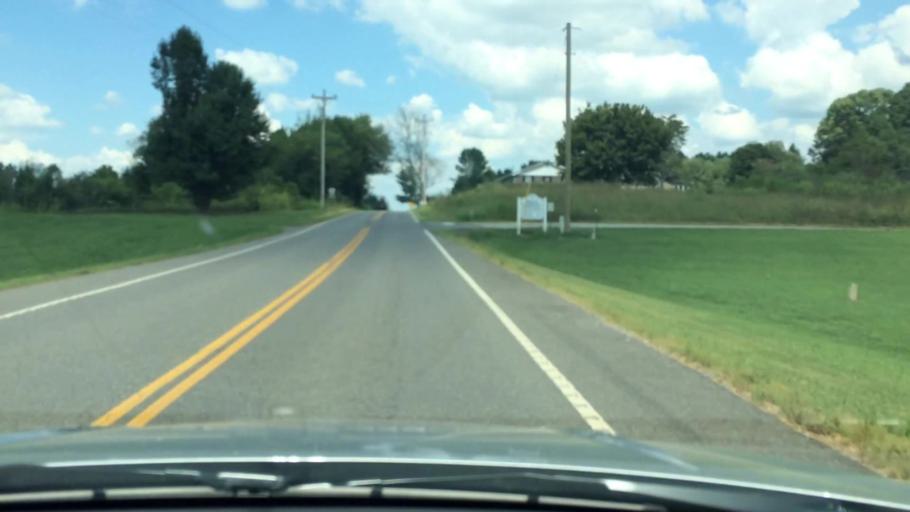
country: US
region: Tennessee
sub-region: McMinn County
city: Englewood
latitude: 35.4918
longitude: -84.5084
